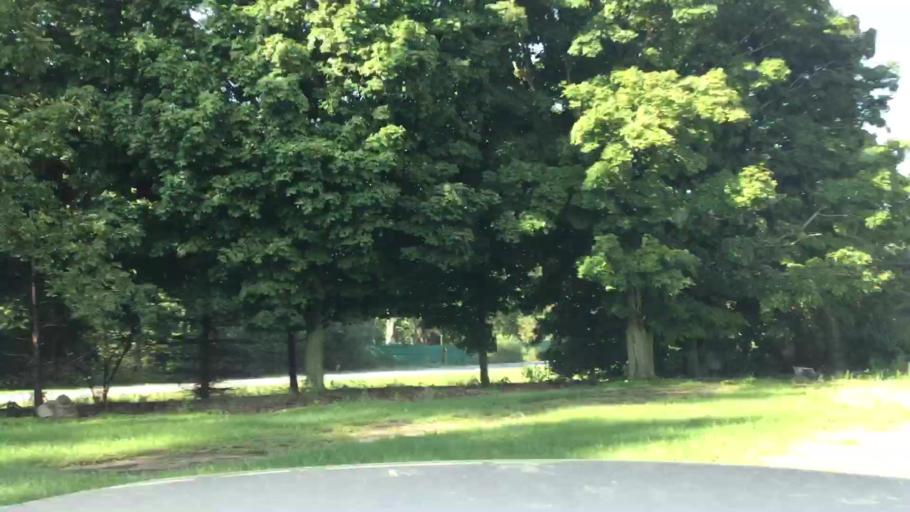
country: US
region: Michigan
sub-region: Lenawee County
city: Manitou Beach-Devils Lake
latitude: 41.9430
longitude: -84.3415
